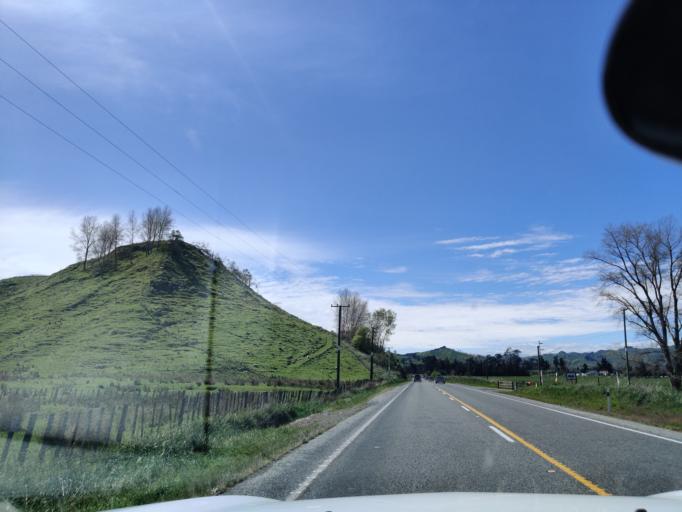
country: NZ
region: Manawatu-Wanganui
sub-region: Ruapehu District
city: Waiouru
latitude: -39.8512
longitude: 175.7320
